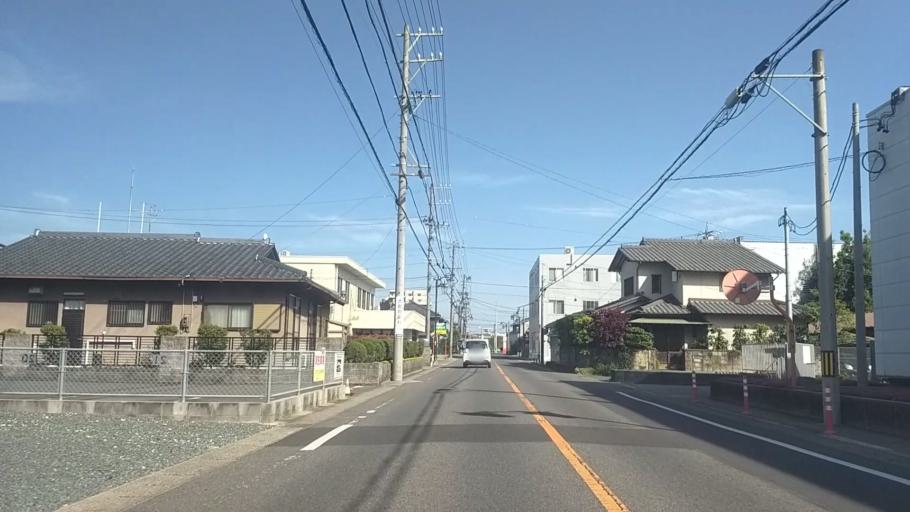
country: JP
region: Aichi
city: Anjo
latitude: 34.9606
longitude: 137.0907
